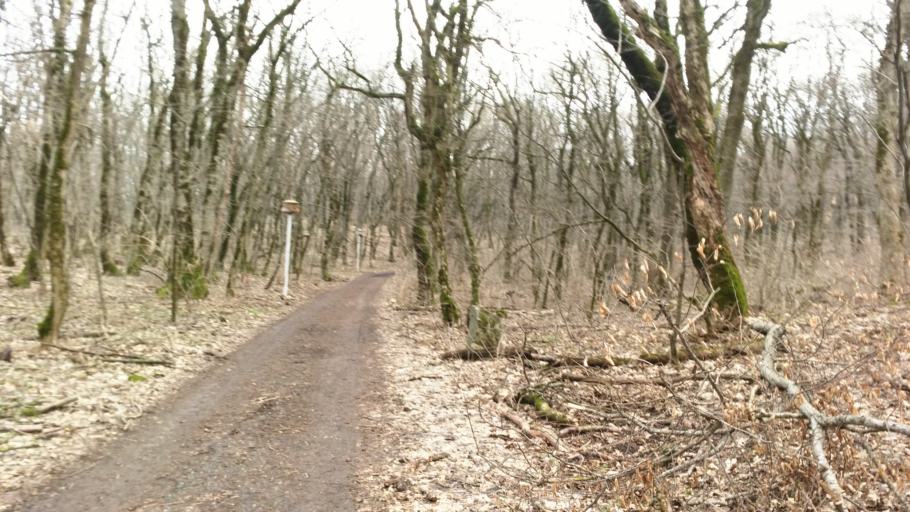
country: RU
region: Stavropol'skiy
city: Zheleznovodsk
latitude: 44.1596
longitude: 43.0399
